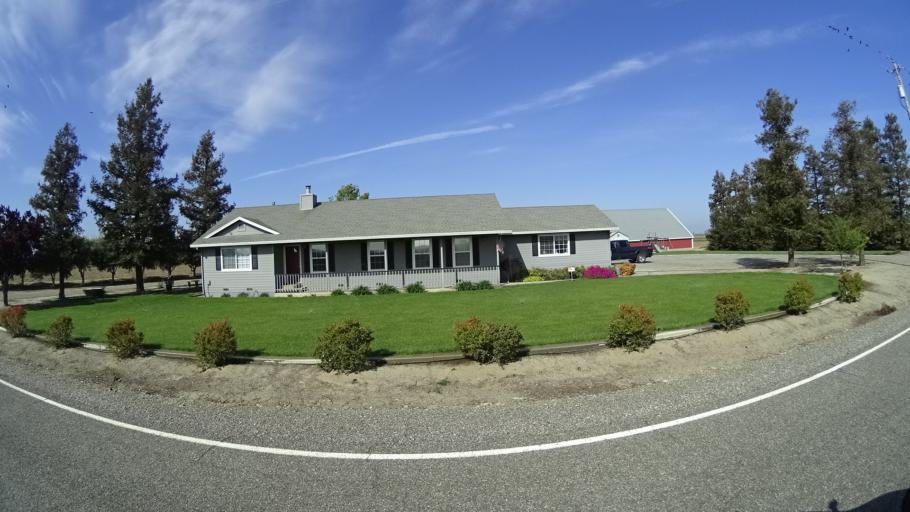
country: US
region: California
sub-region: Glenn County
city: Hamilton City
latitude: 39.5993
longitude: -122.0369
